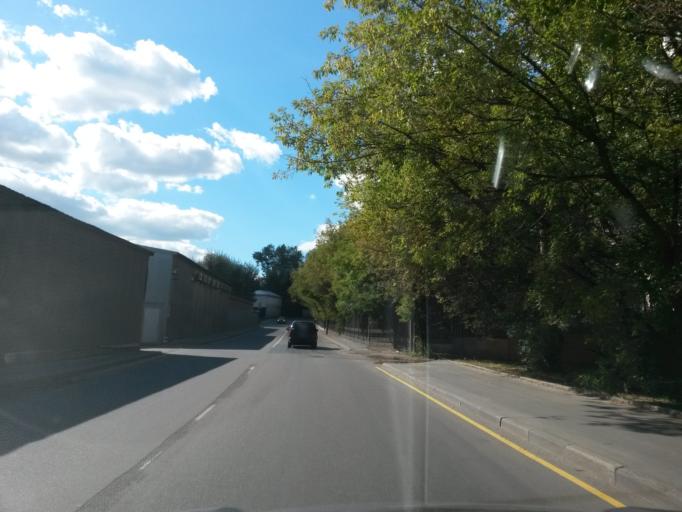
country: RU
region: Moskovskaya
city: Kozhukhovo
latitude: 55.7003
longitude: 37.6784
